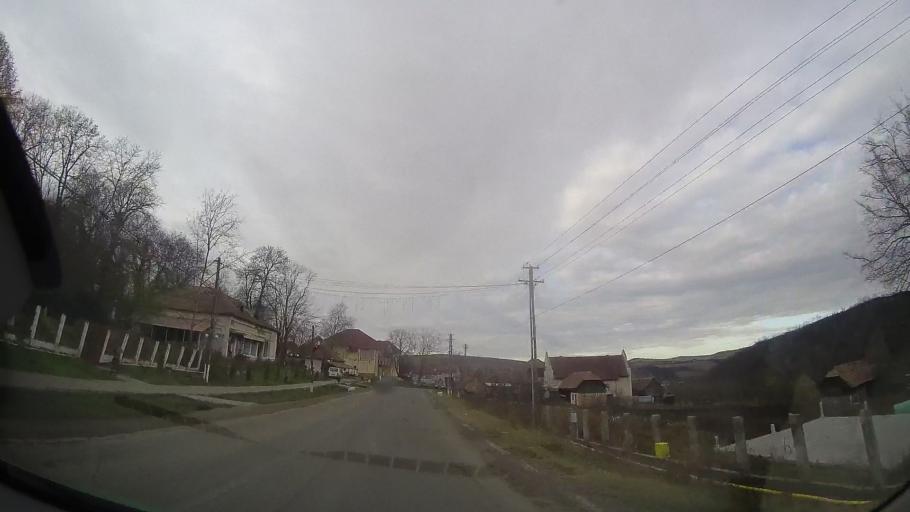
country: RO
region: Bistrita-Nasaud
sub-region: Comuna Silvasu de Campie
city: Silvasu de Campie
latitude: 46.7795
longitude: 24.2945
